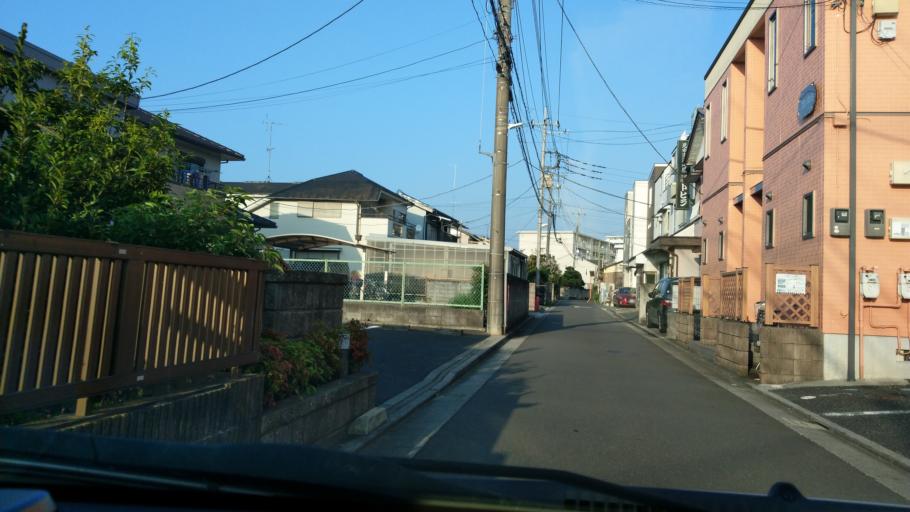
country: JP
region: Saitama
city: Yono
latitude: 35.8578
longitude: 139.6123
